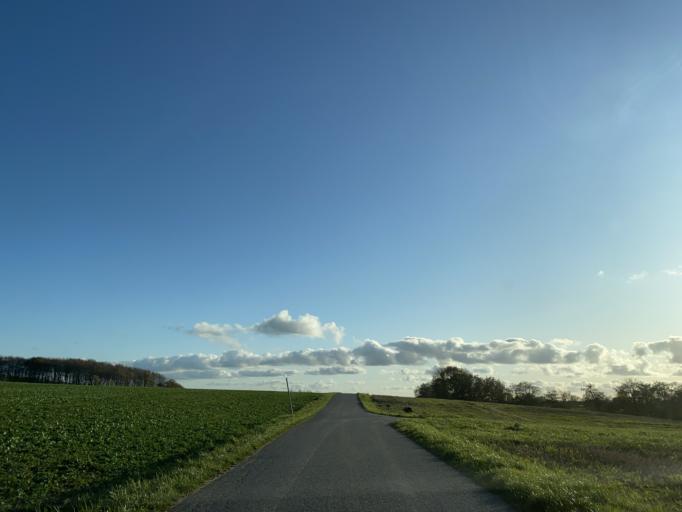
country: DK
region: Central Jutland
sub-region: Viborg Kommune
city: Bjerringbro
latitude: 56.3438
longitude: 9.7146
